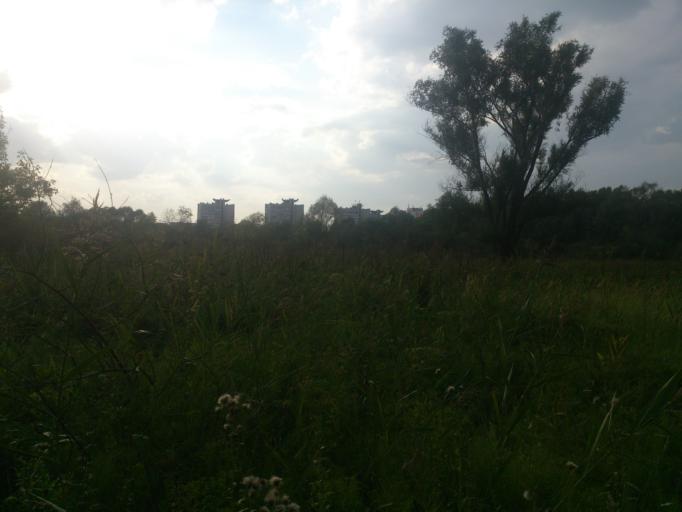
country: RU
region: Ulyanovsk
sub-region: Ulyanovskiy Rayon
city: Ulyanovsk
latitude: 54.3026
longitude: 48.3575
